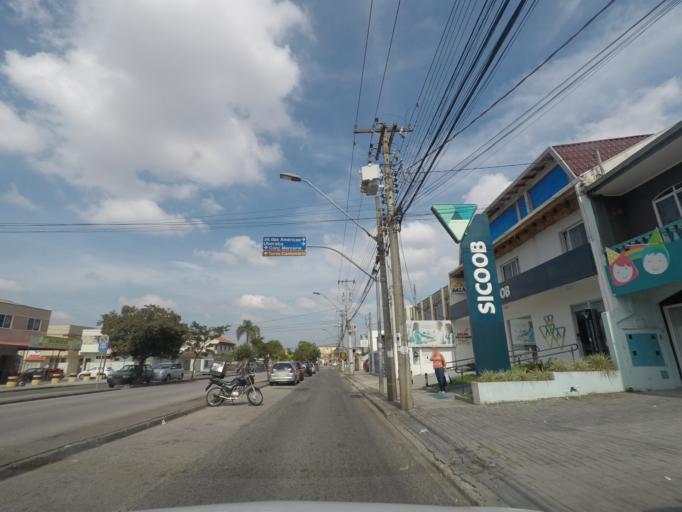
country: BR
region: Parana
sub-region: Pinhais
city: Pinhais
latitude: -25.4625
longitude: -49.2111
